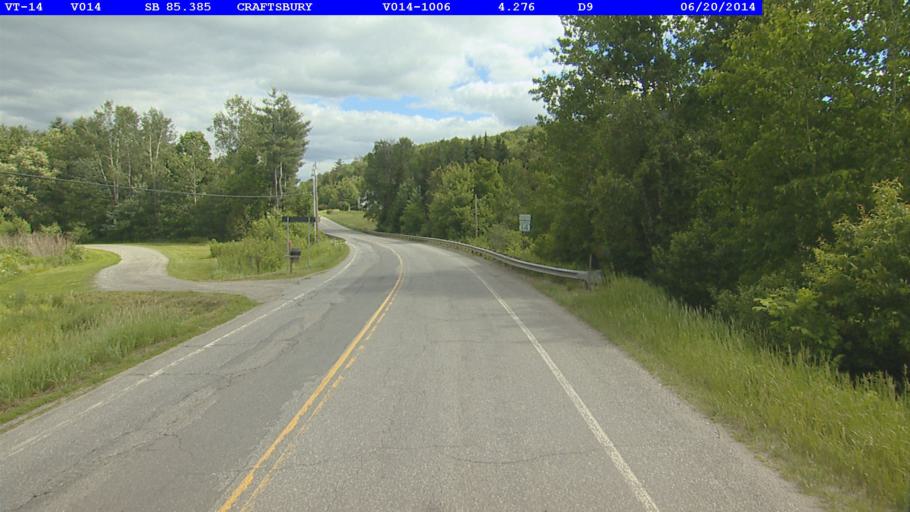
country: US
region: Vermont
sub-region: Caledonia County
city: Hardwick
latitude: 44.6524
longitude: -72.4059
